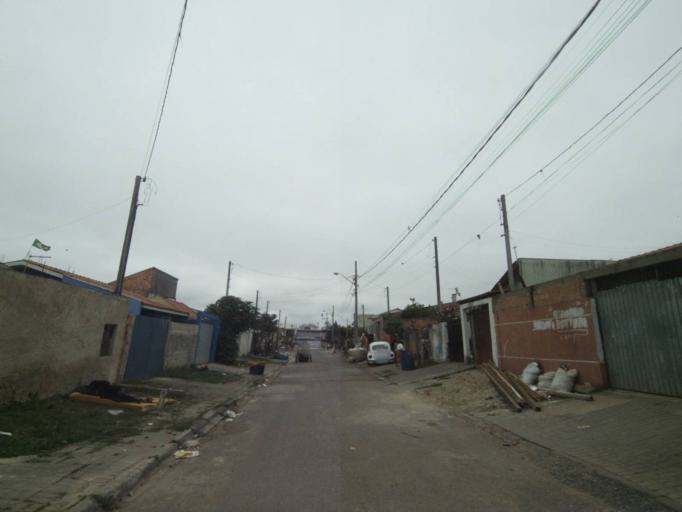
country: BR
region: Parana
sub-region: Curitiba
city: Curitiba
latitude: -25.4656
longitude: -49.2674
